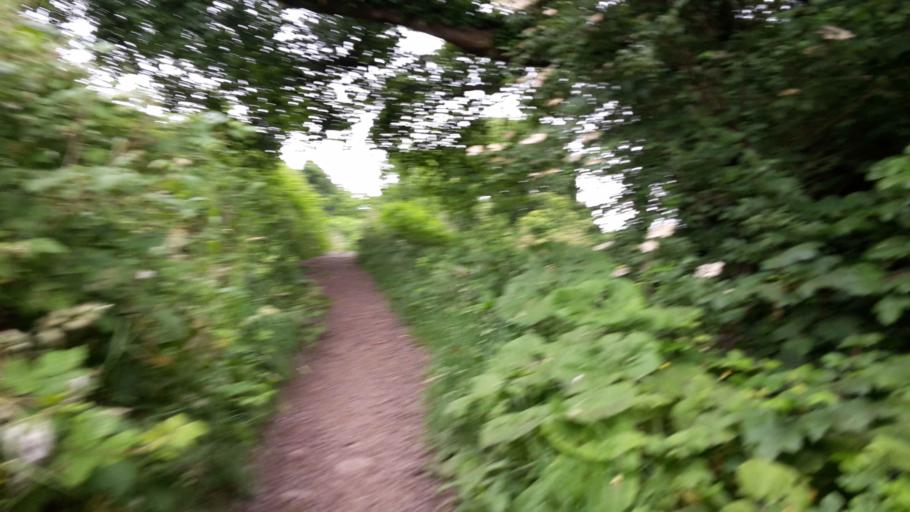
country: GB
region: Scotland
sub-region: South Lanarkshire
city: Uddingston
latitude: 55.8093
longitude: -4.0959
